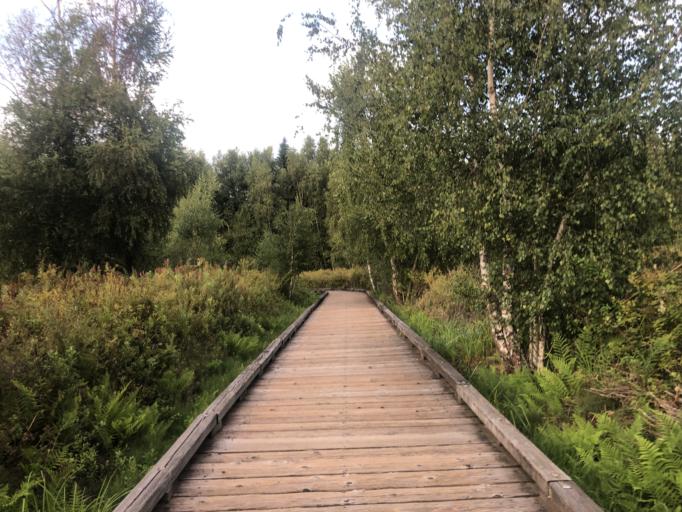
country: US
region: Washington
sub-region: King County
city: Newport
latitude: 47.5883
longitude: -122.1879
